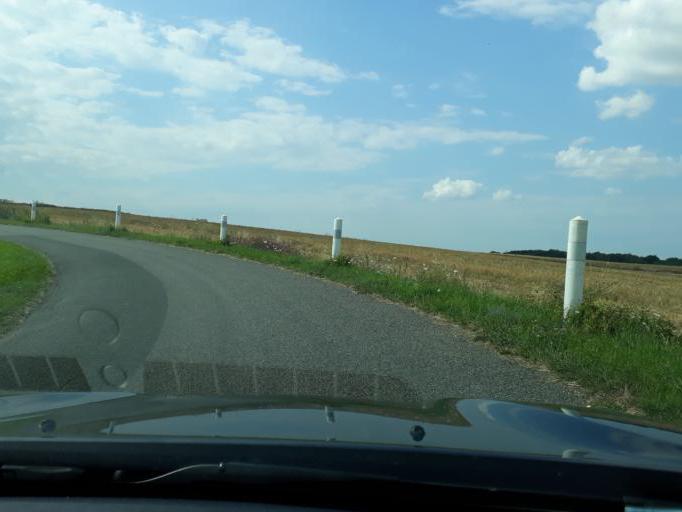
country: FR
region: Centre
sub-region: Departement du Cher
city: Jouet-sur-l'Aubois
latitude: 47.0211
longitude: 2.9091
